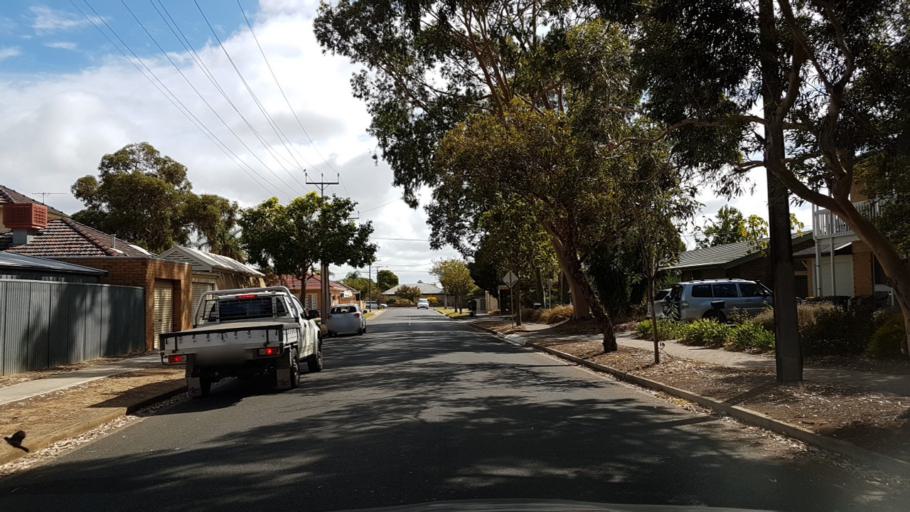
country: AU
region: South Australia
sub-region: Marion
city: Plympton Park
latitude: -34.9916
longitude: 138.5511
